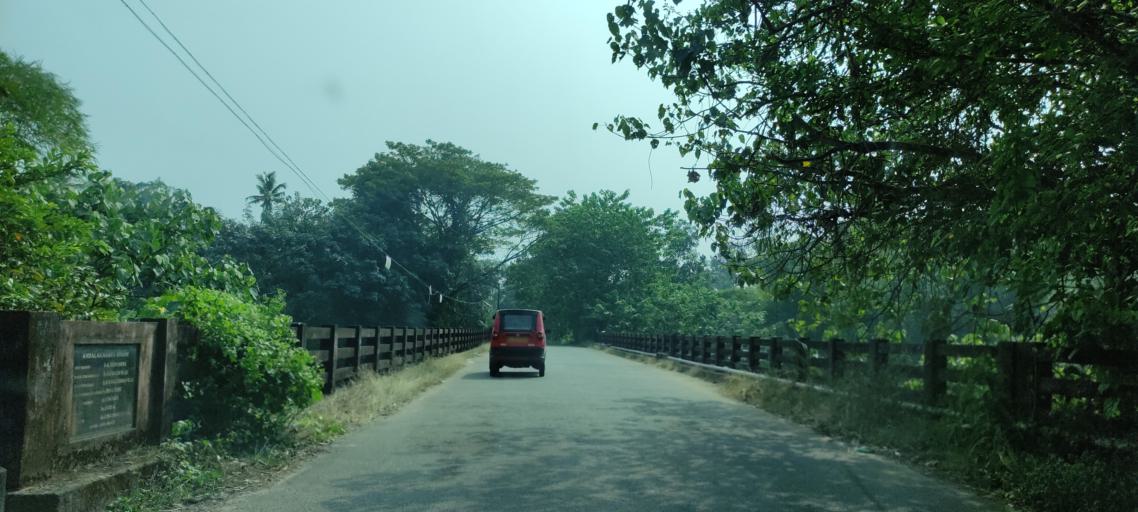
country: IN
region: Kerala
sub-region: Pattanamtitta
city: Adur
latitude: 9.2291
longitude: 76.7125
